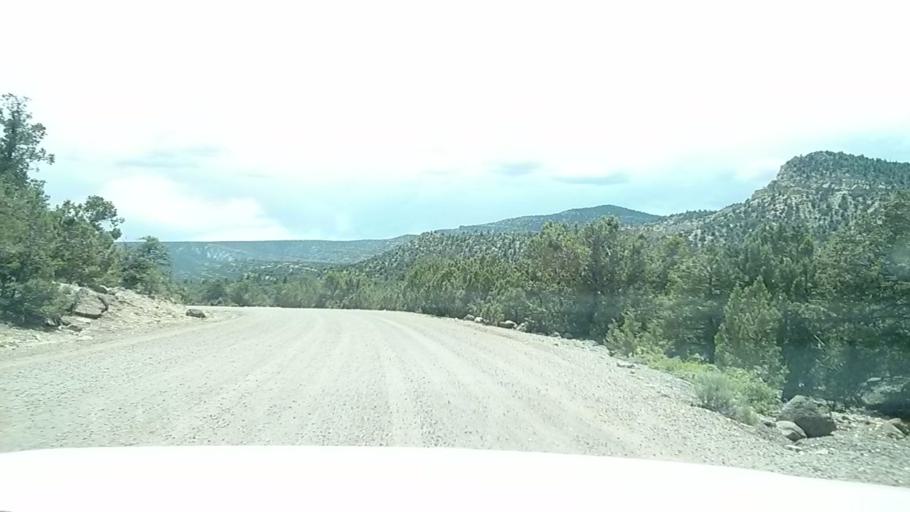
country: US
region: Utah
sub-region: Wayne County
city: Loa
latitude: 37.9077
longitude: -111.6718
